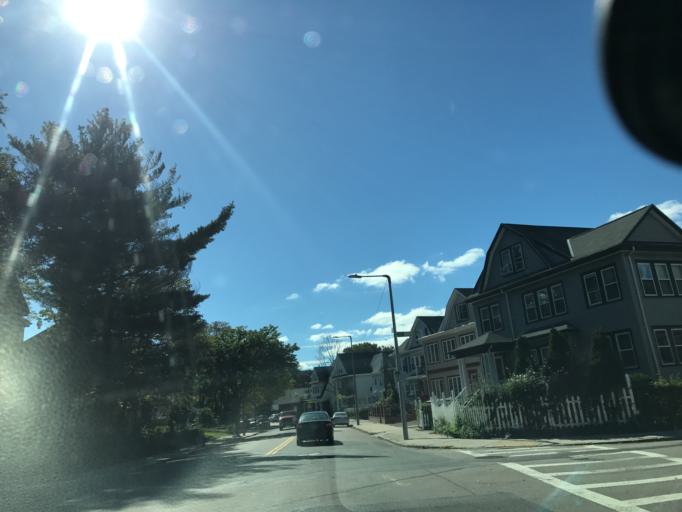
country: US
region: Massachusetts
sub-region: Suffolk County
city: South Boston
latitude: 42.2928
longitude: -71.0574
